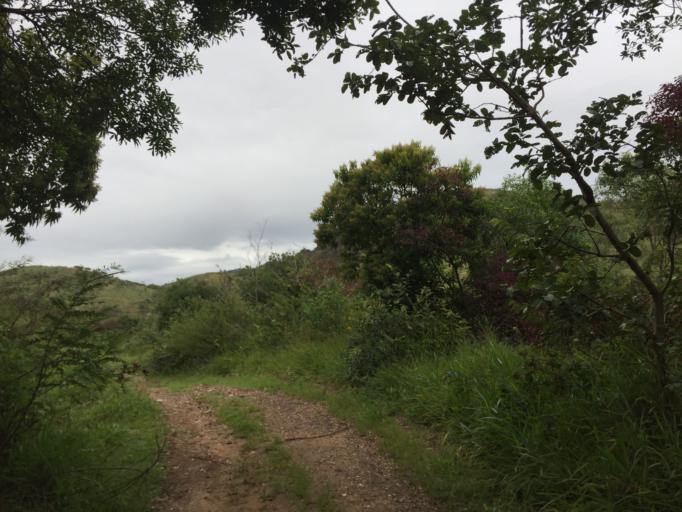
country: BR
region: Minas Gerais
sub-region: Sao Joao Del Rei
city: Sao Joao del Rei
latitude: -21.1273
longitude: -44.2674
